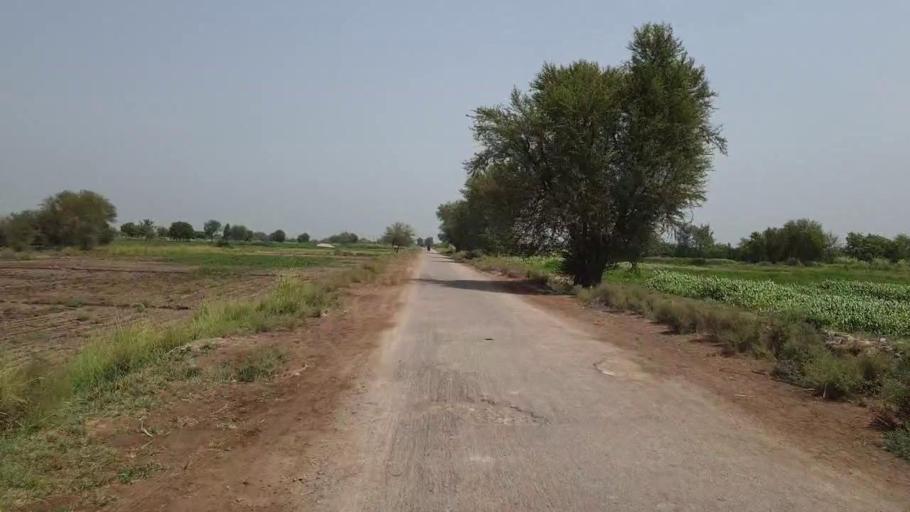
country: PK
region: Sindh
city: Nawabshah
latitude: 26.2635
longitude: 68.3180
